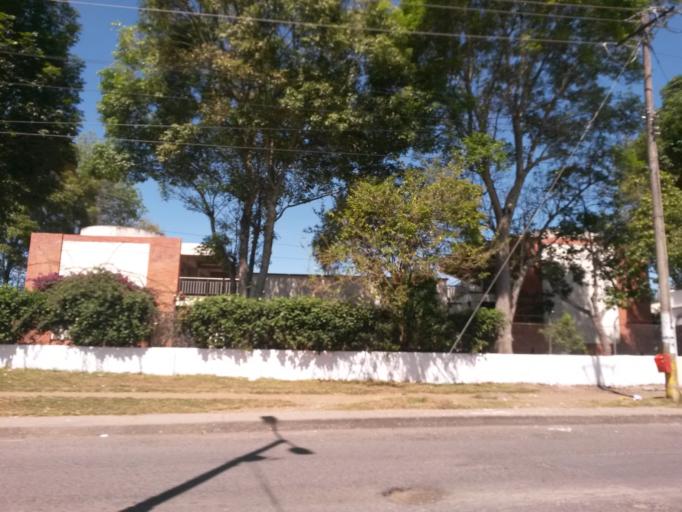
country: CO
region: Cauca
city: Popayan
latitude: 2.4514
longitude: -76.6296
